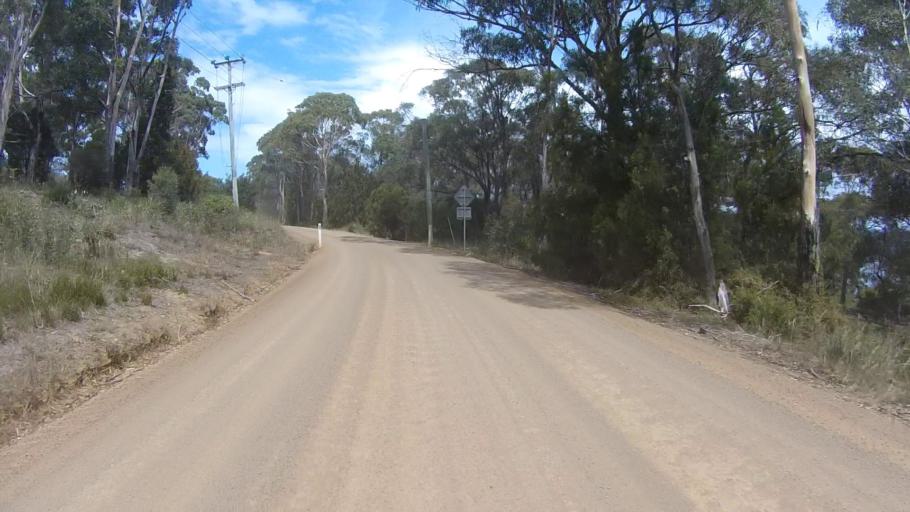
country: AU
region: Tasmania
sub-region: Kingborough
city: Blackmans Bay
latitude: -43.0470
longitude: 147.3073
